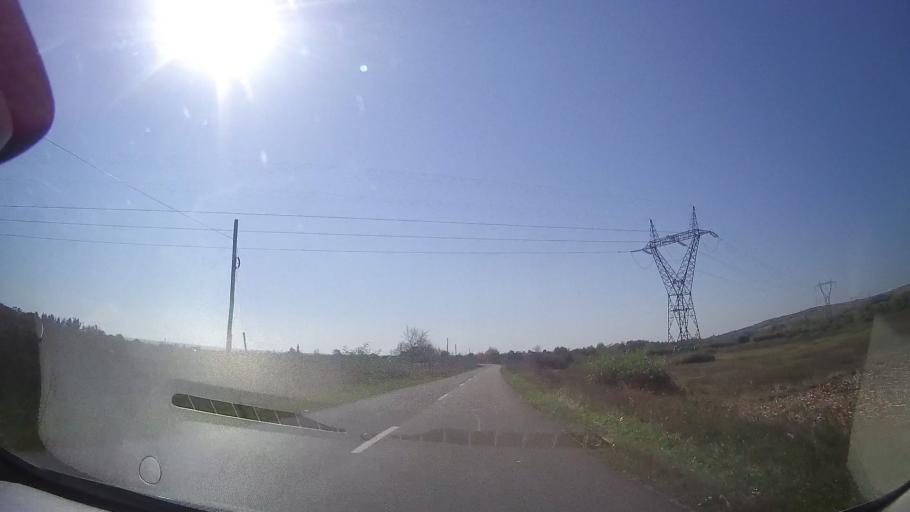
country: RO
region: Timis
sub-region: Comuna Bethausen
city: Bethausen
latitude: 45.8443
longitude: 21.9611
